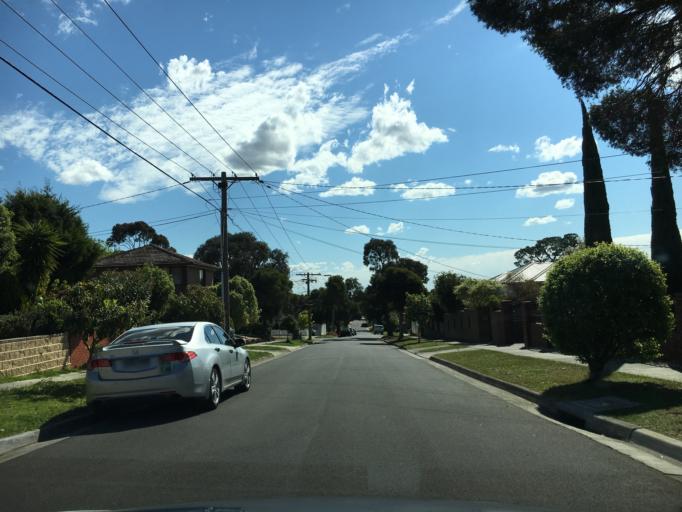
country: AU
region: Victoria
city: Clayton
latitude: -37.8943
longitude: 145.1188
